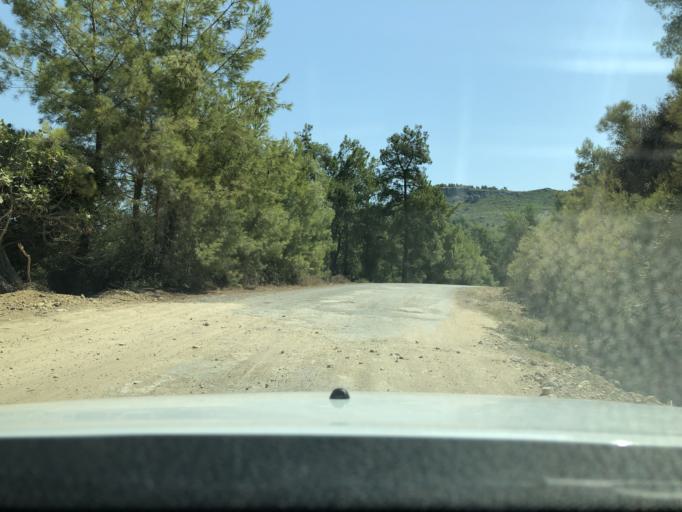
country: TR
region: Antalya
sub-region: Manavgat
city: Manavgat
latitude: 36.8259
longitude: 31.5111
